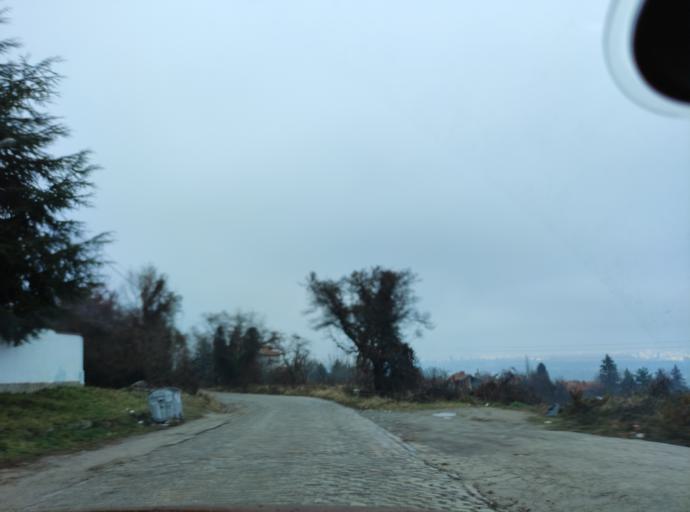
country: BG
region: Sofia-Capital
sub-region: Stolichna Obshtina
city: Sofia
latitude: 42.6238
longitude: 23.3090
